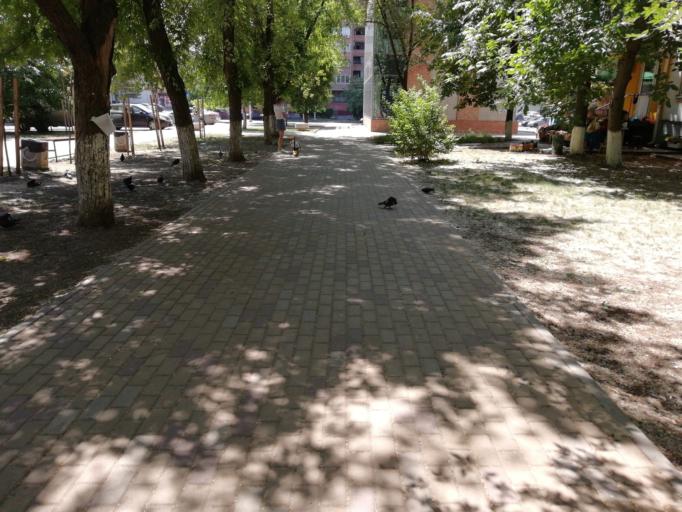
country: RU
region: Rostov
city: Severnyy
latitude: 47.2836
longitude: 39.7115
